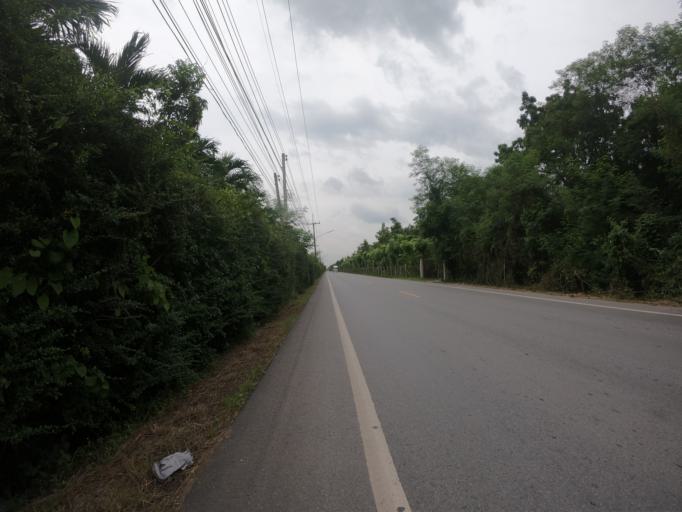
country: TH
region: Pathum Thani
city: Nong Suea
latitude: 14.0616
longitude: 100.8716
